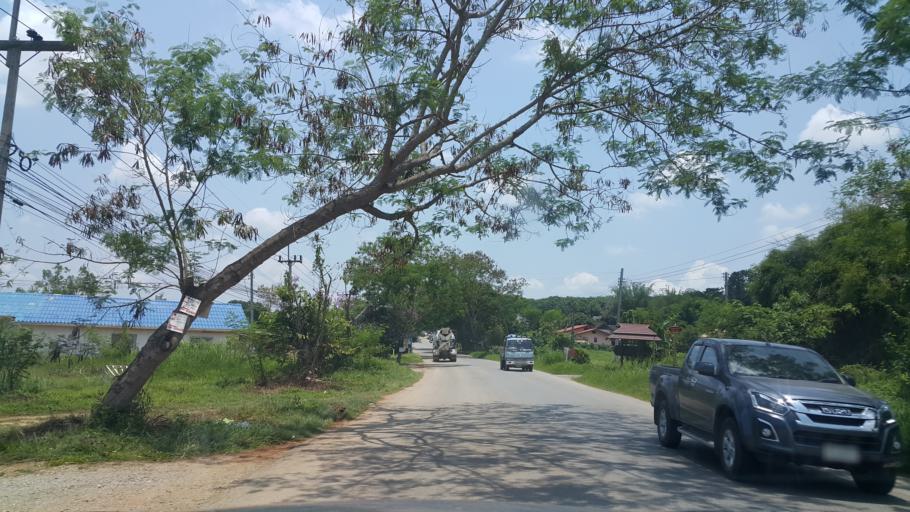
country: TH
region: Chiang Rai
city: Chiang Rai
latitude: 19.9401
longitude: 99.8072
